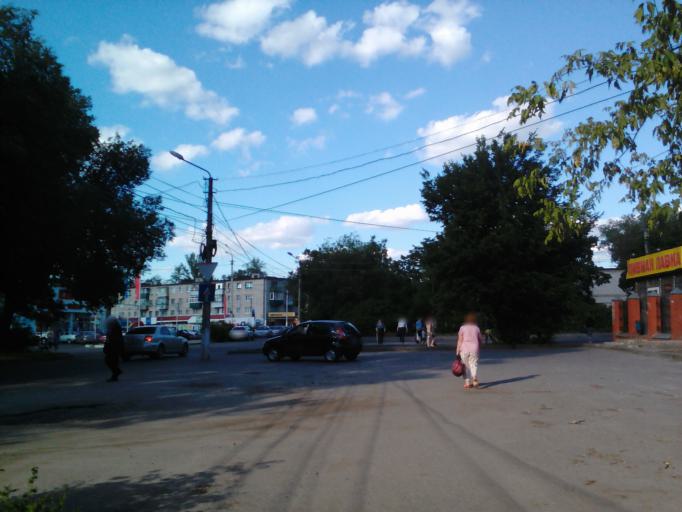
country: RU
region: Kursk
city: Voroshnevo
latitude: 51.6687
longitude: 36.0735
